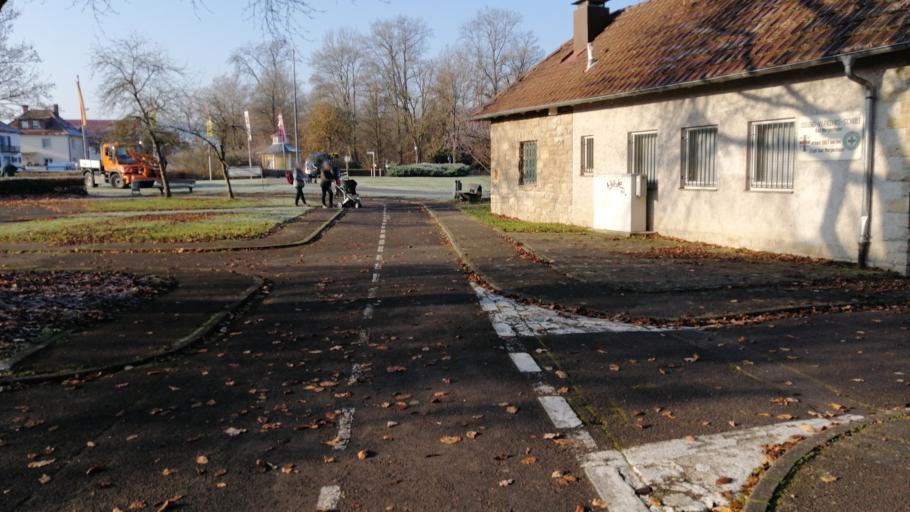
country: DE
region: Baden-Wuerttemberg
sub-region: Regierungsbezirk Stuttgart
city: Bad Mergentheim
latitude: 49.4919
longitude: 9.7832
